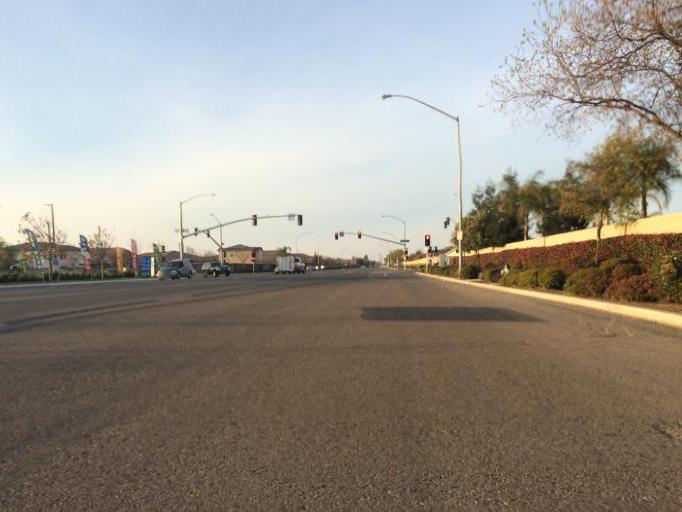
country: US
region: California
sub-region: Fresno County
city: Tarpey Village
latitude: 36.7786
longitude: -119.6730
